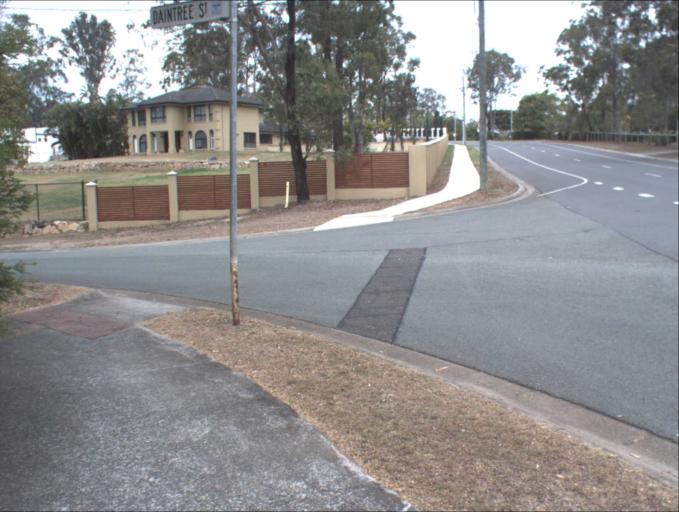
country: AU
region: Queensland
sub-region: Logan
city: Beenleigh
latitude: -27.6687
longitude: 153.2221
